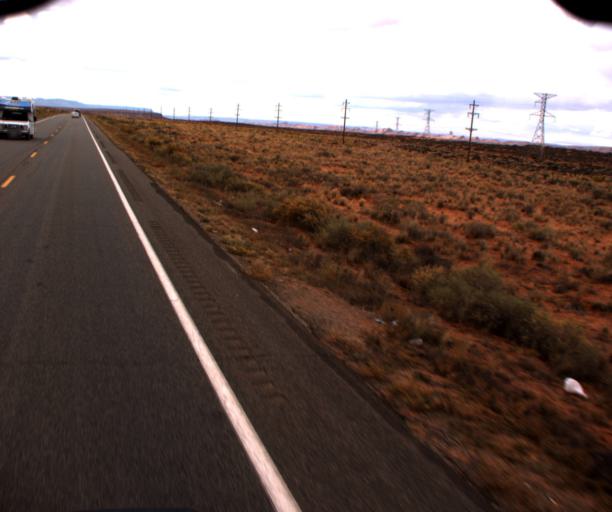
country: US
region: Arizona
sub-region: Navajo County
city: Kayenta
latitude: 36.7994
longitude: -109.9280
